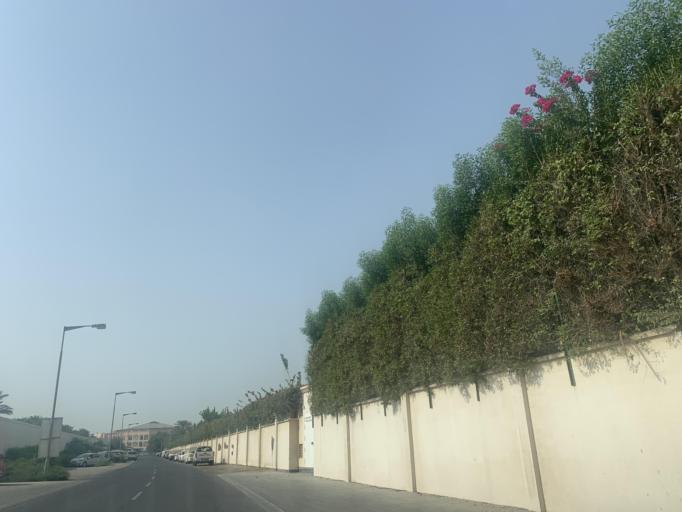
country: BH
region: Manama
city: Jidd Hafs
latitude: 26.2135
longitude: 50.4739
